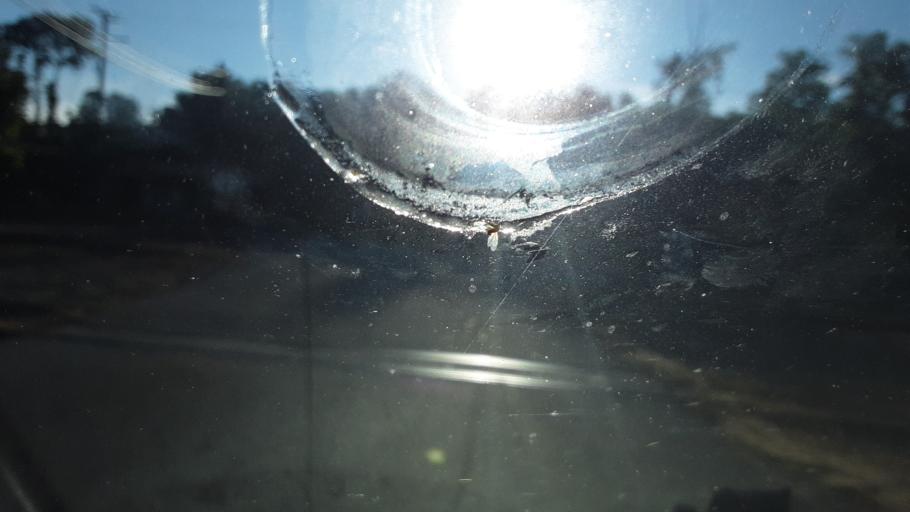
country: US
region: Virginia
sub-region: Pittsylvania County
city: Chatham
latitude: 36.8208
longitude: -79.4048
